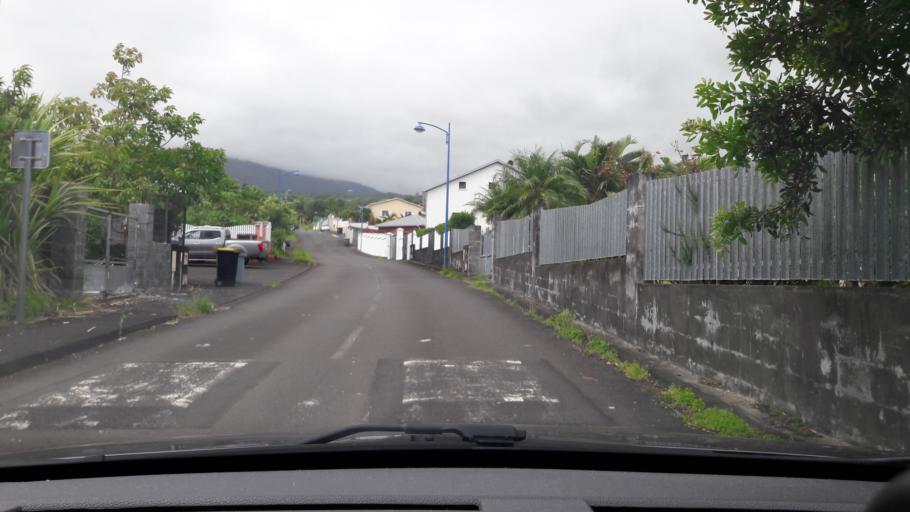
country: RE
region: Reunion
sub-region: Reunion
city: Saint-Benoit
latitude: -21.0932
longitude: 55.7035
